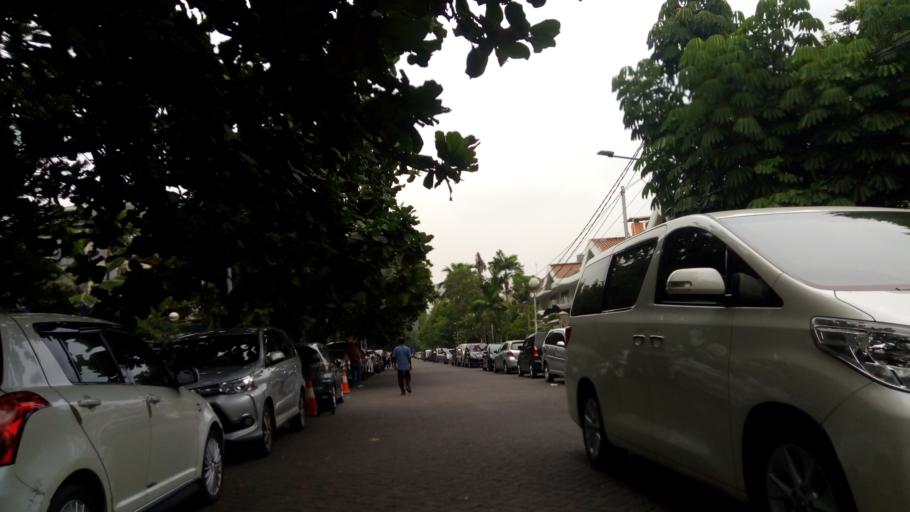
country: ID
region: Jakarta Raya
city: Jakarta
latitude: -6.1540
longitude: 106.8417
